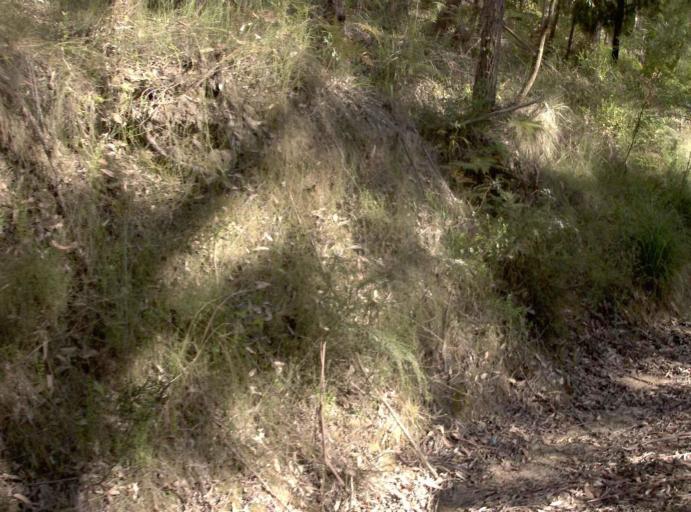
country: AU
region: Victoria
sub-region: East Gippsland
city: Lakes Entrance
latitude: -37.6307
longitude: 148.5039
